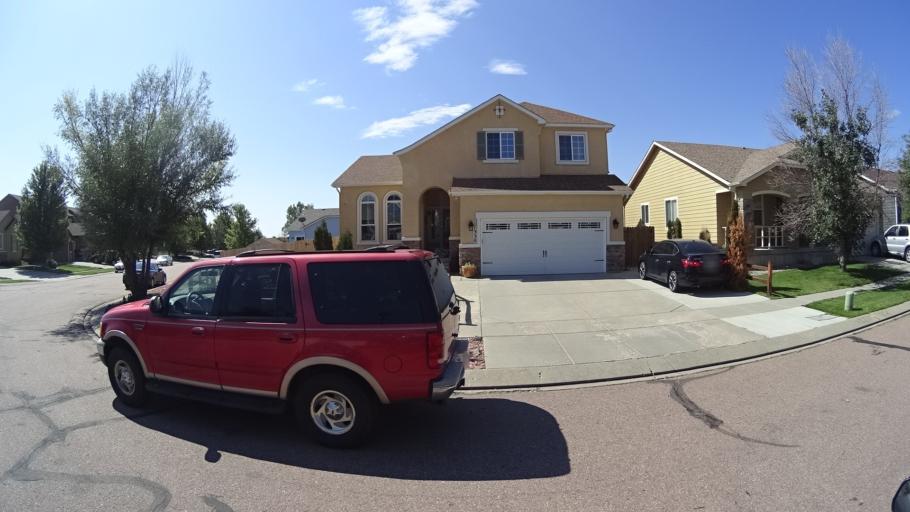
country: US
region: Colorado
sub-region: El Paso County
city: Cimarron Hills
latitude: 38.9236
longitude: -104.6973
